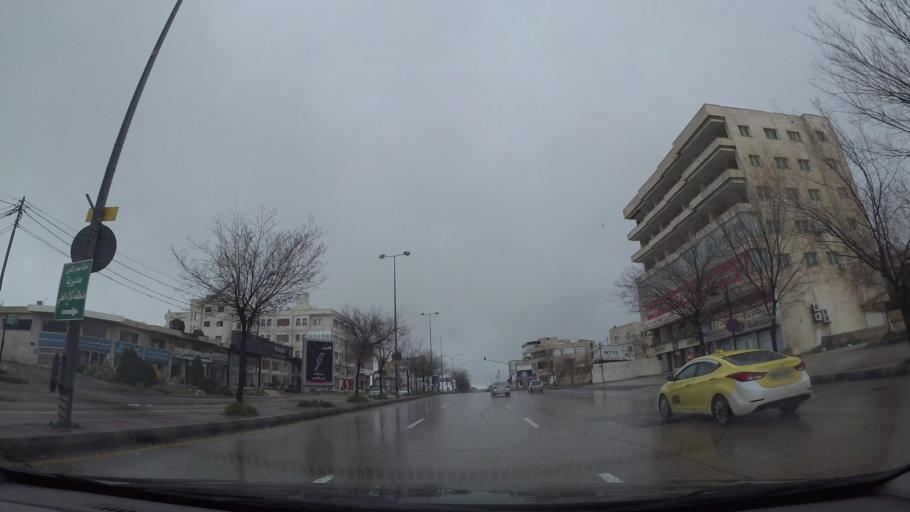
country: JO
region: Amman
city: Wadi as Sir
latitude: 31.9762
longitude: 35.8515
